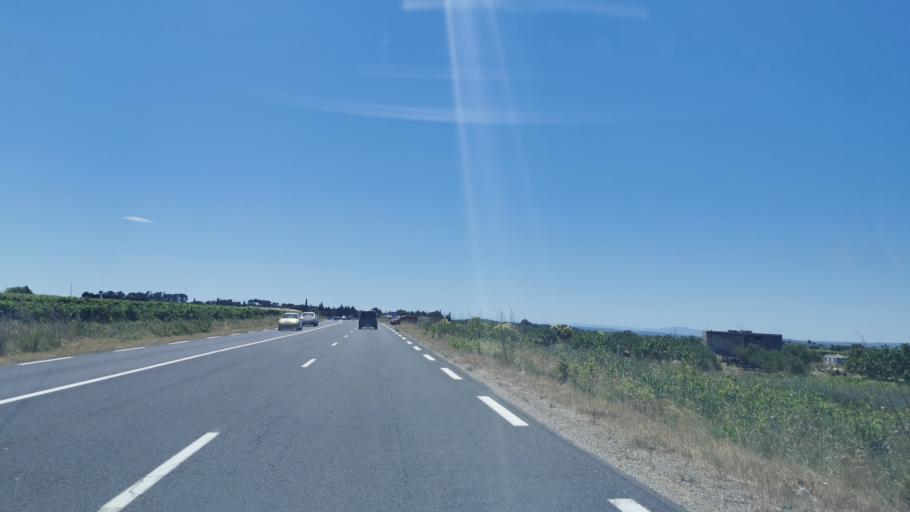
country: FR
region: Languedoc-Roussillon
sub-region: Departement de l'Herault
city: Colombiers
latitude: 43.3025
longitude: 3.1558
